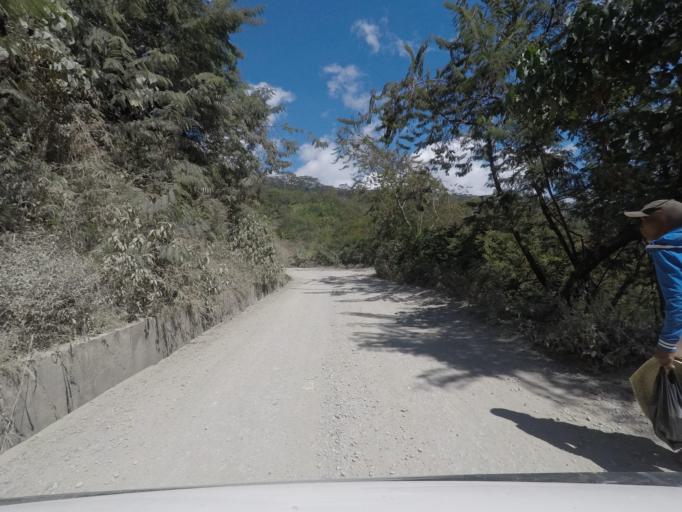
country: TL
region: Ermera
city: Gleno
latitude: -8.7462
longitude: 125.3896
